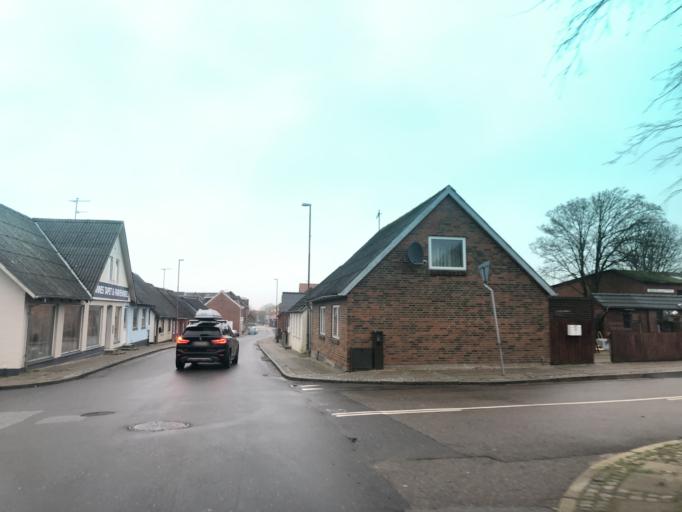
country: DK
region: North Denmark
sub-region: Thisted Kommune
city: Hurup
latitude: 56.7476
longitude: 8.4204
